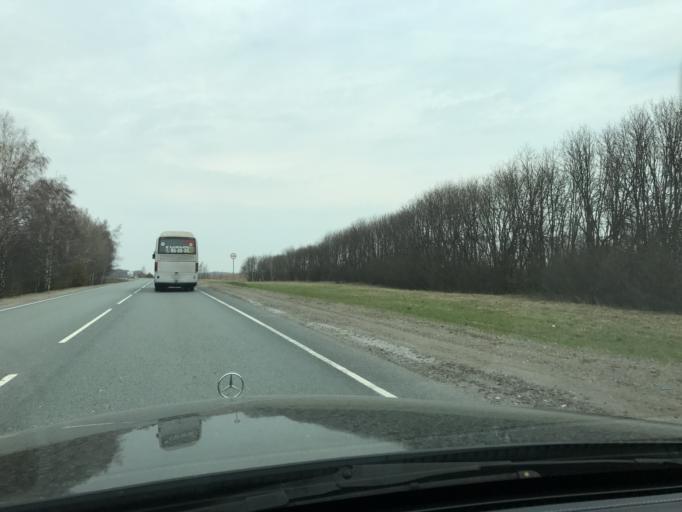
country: RU
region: Vladimir
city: Suzdal'
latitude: 56.3536
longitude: 40.4723
